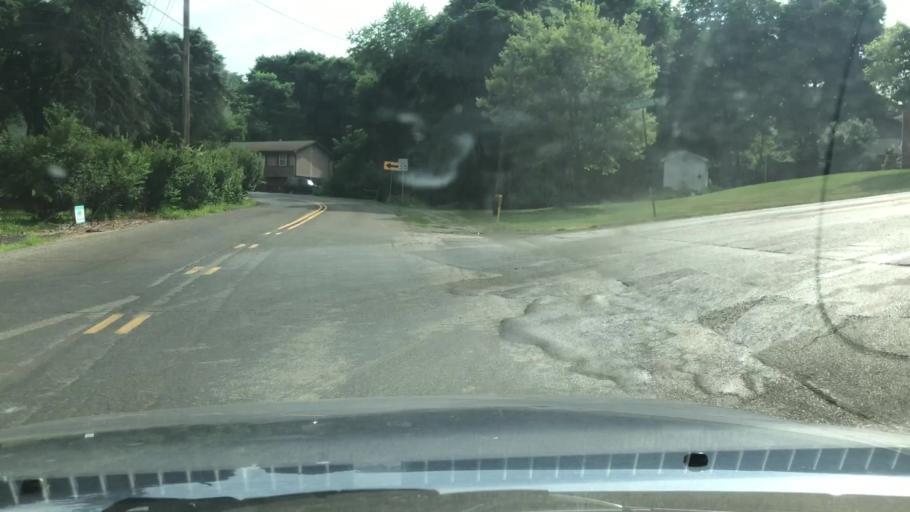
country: US
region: Pennsylvania
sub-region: Butler County
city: Meadowood
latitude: 40.8454
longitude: -79.9007
